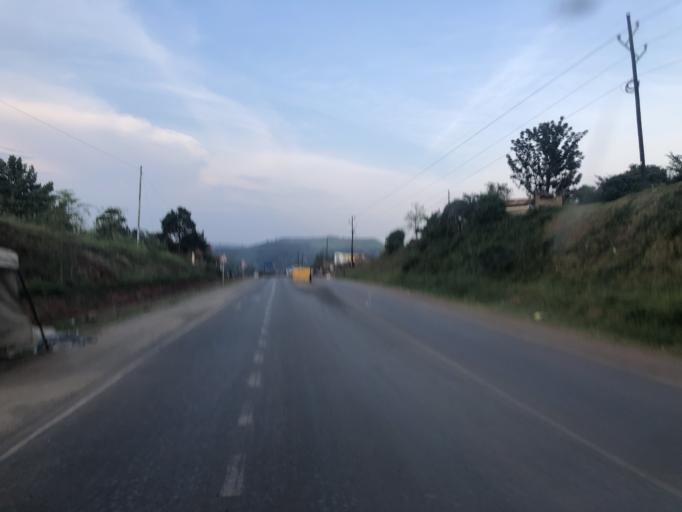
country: UG
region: Central Region
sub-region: Mpigi District
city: Mpigi
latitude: 0.2184
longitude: 32.3321
